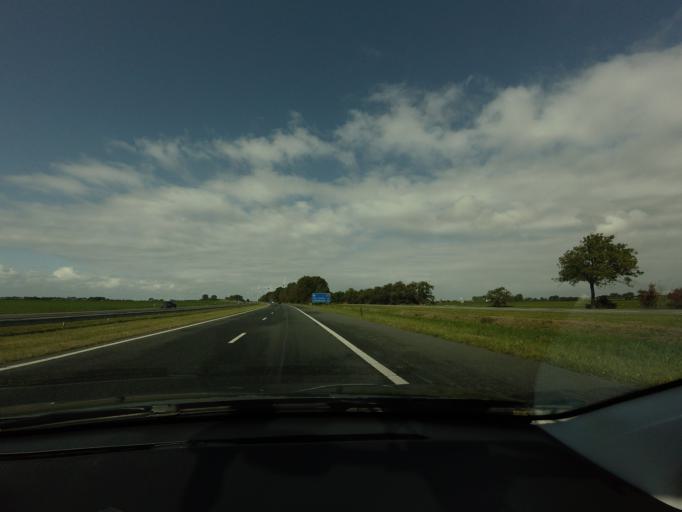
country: NL
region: Friesland
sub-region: Sudwest Fryslan
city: Makkum
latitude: 53.0850
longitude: 5.4591
